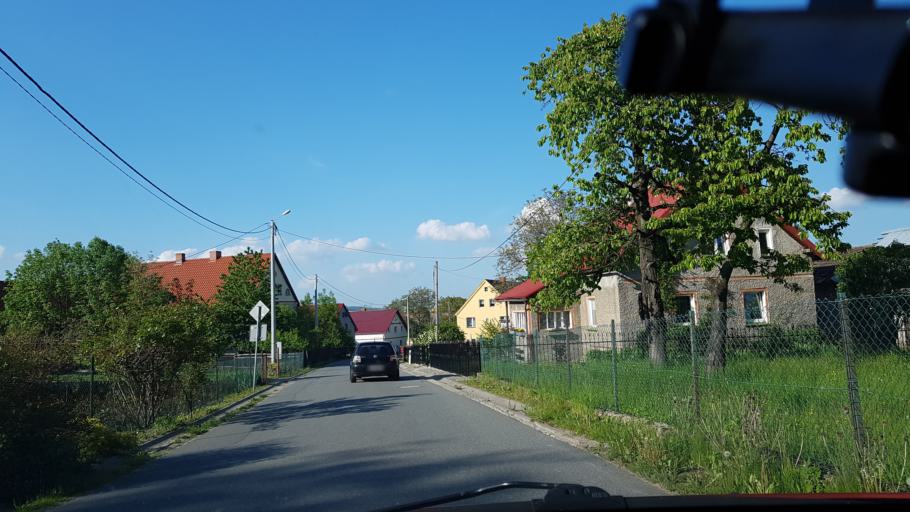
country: PL
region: Lower Silesian Voivodeship
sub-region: Powiat dzierzoniowski
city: Ostroszowice
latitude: 50.5938
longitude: 16.6519
